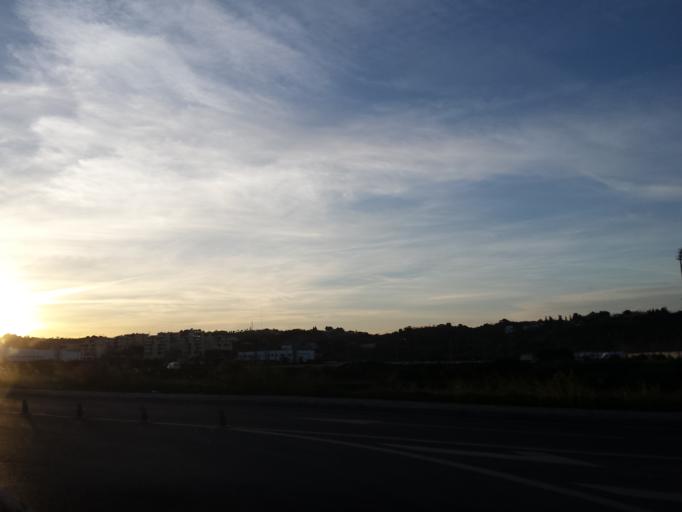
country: PT
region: Faro
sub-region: Lagos
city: Lagos
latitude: 37.1145
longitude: -8.6761
